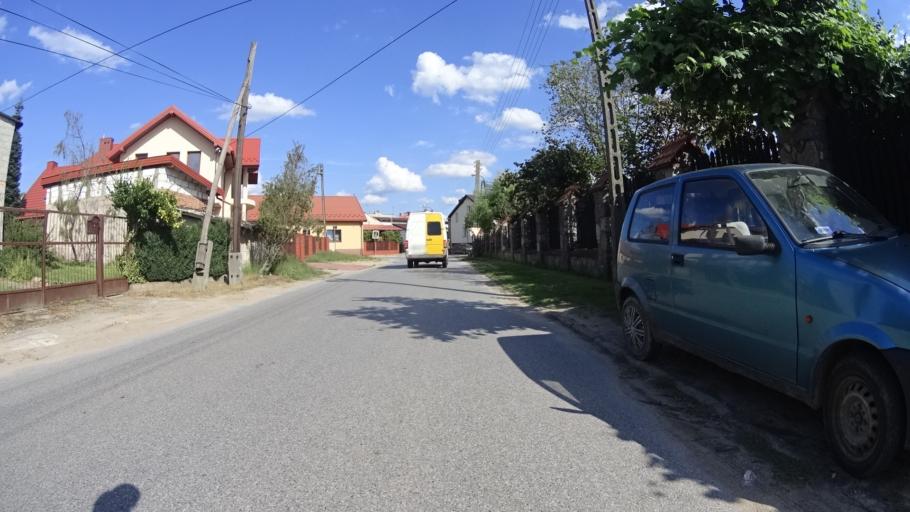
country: PL
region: Masovian Voivodeship
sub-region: Powiat grojecki
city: Mogielnica
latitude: 51.6941
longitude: 20.7201
